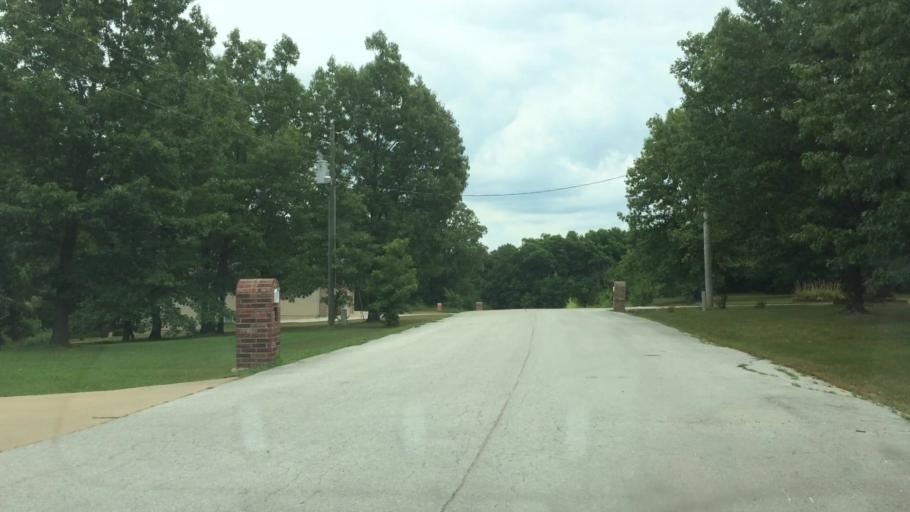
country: US
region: Missouri
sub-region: Greene County
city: Strafford
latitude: 37.2790
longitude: -93.0492
